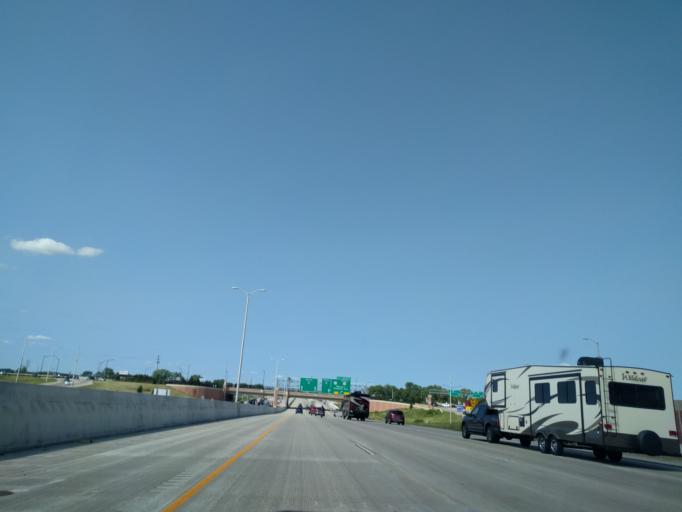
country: US
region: Wisconsin
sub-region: Brown County
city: Howard
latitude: 44.5216
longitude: -88.0820
